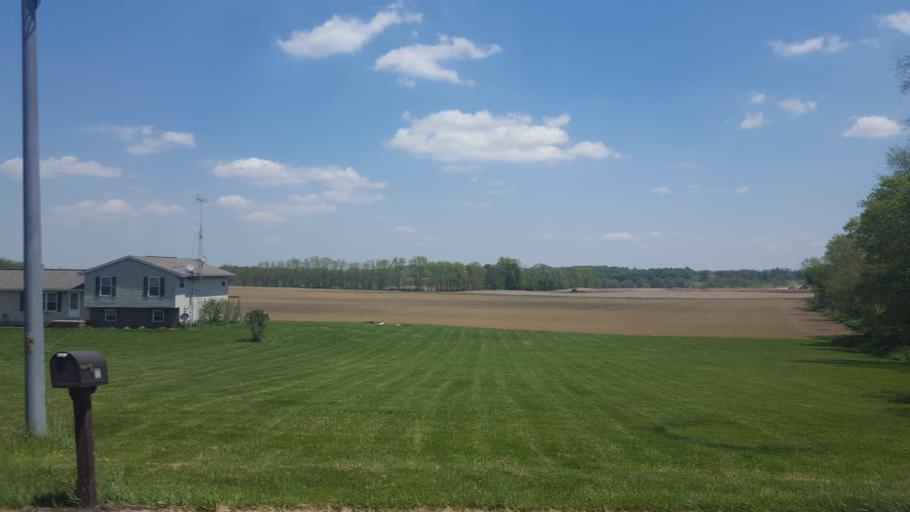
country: US
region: Ohio
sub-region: Knox County
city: Gambier
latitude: 40.3190
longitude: -82.4082
